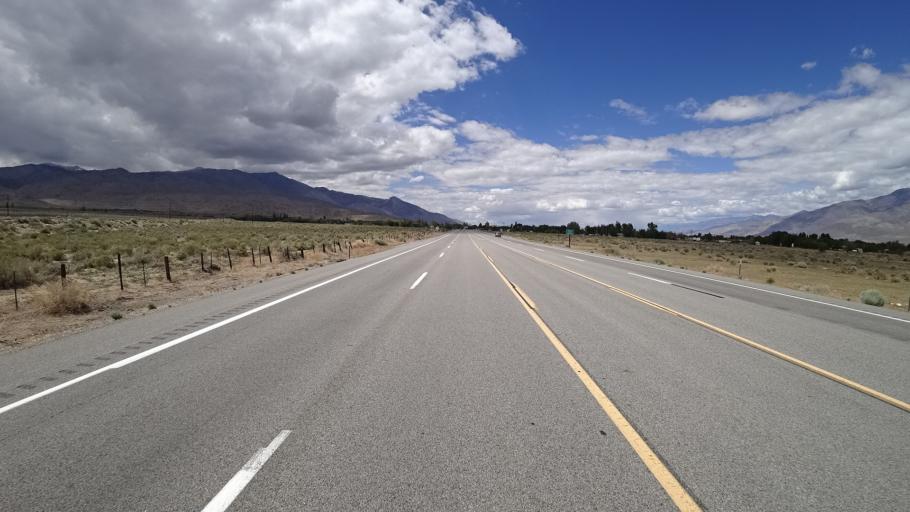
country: US
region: California
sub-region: Inyo County
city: Big Pine
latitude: 37.1520
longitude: -118.2859
